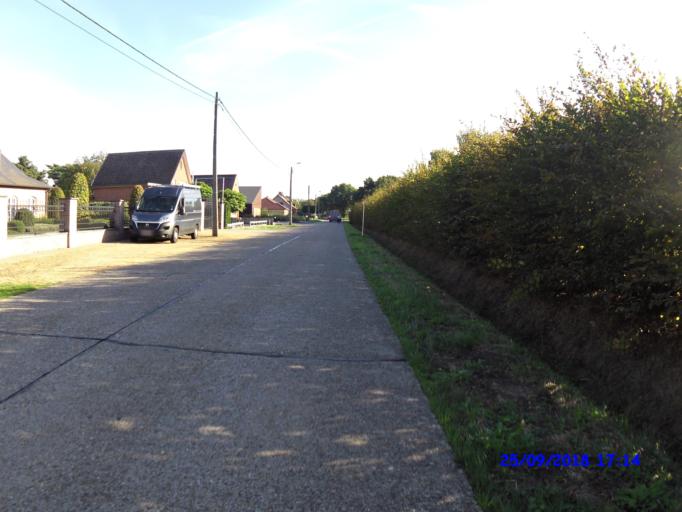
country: BE
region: Flanders
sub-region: Provincie Vlaams-Brabant
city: Begijnendijk
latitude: 51.0331
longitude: 4.7933
